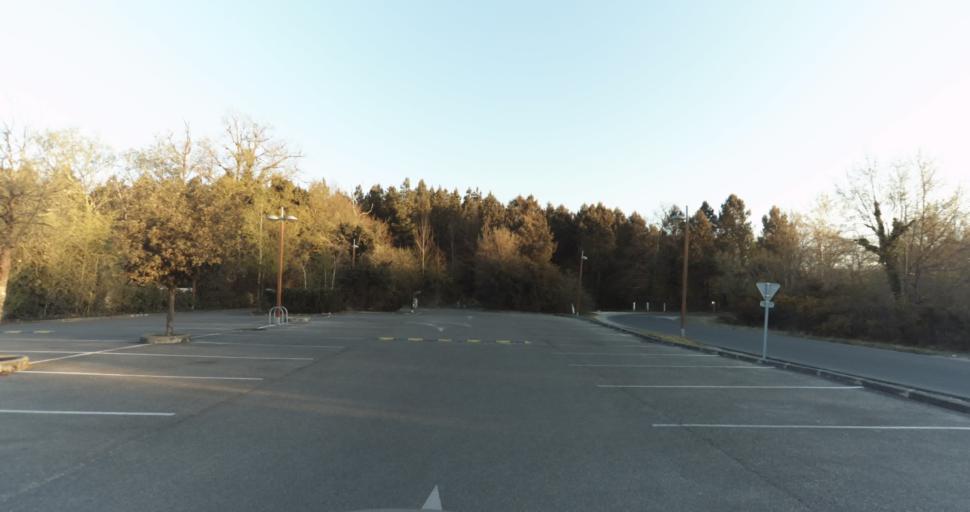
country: FR
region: Aquitaine
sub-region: Departement de la Gironde
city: Martignas-sur-Jalle
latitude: 44.8116
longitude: -0.7529
